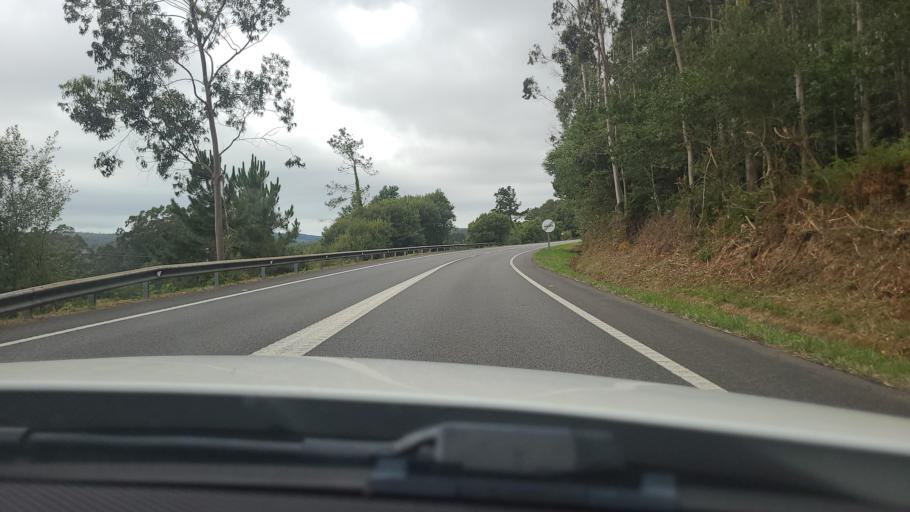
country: ES
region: Galicia
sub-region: Provincia da Coruna
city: Cee
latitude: 42.9974
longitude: -9.1790
